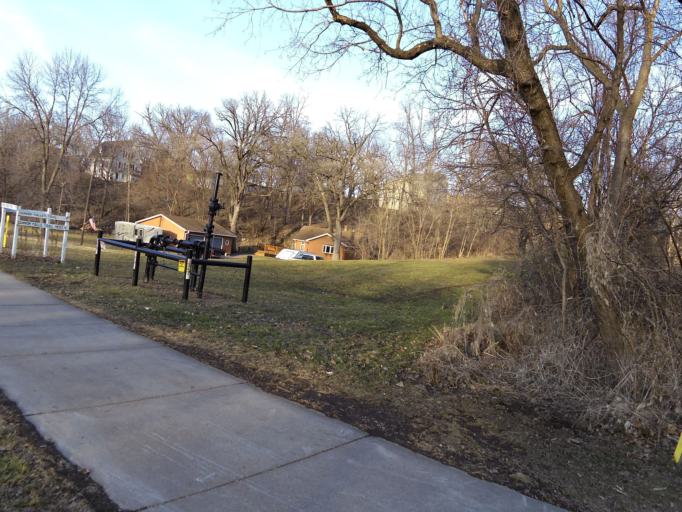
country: US
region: Minnesota
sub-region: Goodhue County
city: Cannon Falls
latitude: 44.5098
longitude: -92.9042
